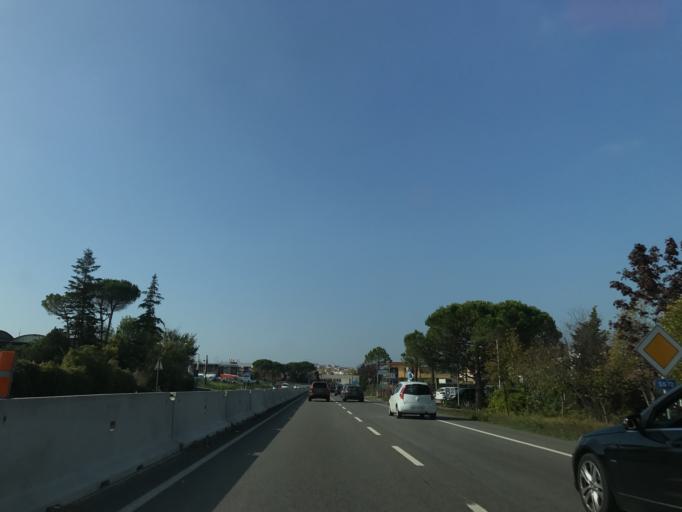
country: IT
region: Emilia-Romagna
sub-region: Provincia di Rimini
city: Cerasolo
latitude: 43.9898
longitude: 12.5316
